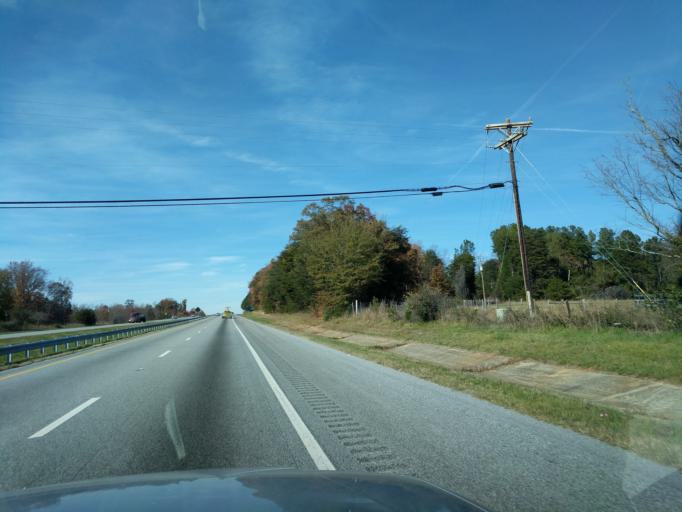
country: US
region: South Carolina
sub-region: Spartanburg County
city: Inman
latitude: 35.1288
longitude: -82.0978
